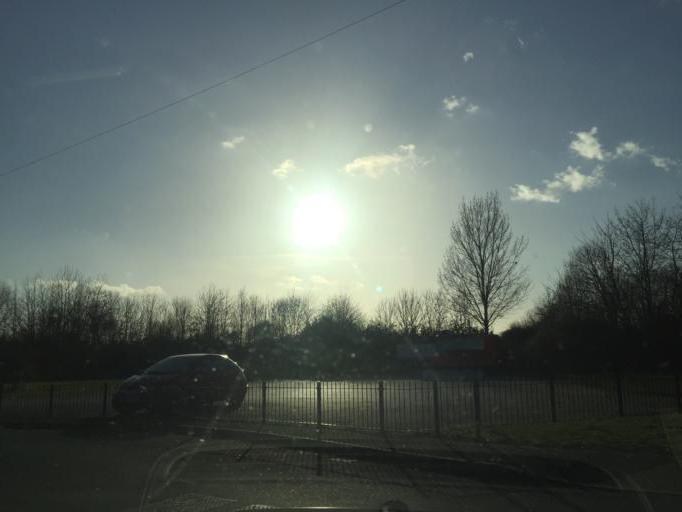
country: GB
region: England
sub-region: Warwickshire
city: Harbury
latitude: 52.1972
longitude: -1.4882
